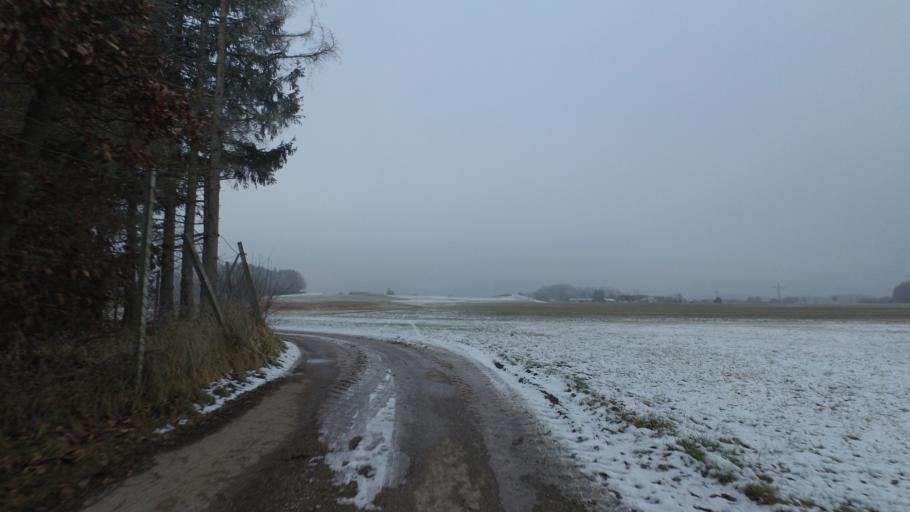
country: DE
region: Bavaria
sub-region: Upper Bavaria
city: Nussdorf
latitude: 47.8850
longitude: 12.5721
